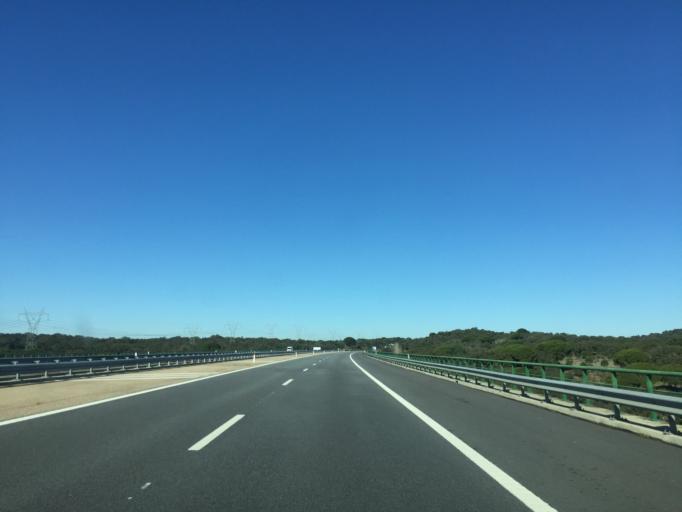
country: PT
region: Setubal
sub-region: Alcacer do Sal
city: Alcacer do Sal
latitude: 38.4939
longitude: -8.5662
